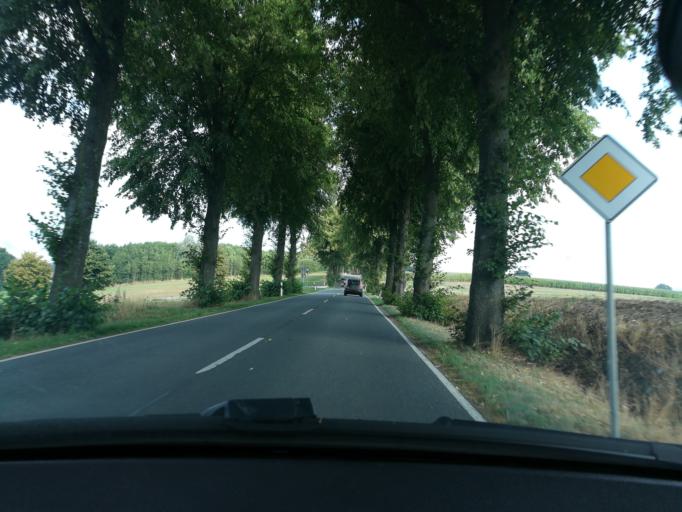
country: DE
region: North Rhine-Westphalia
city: Borgholzhausen
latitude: 52.1436
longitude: 8.3327
